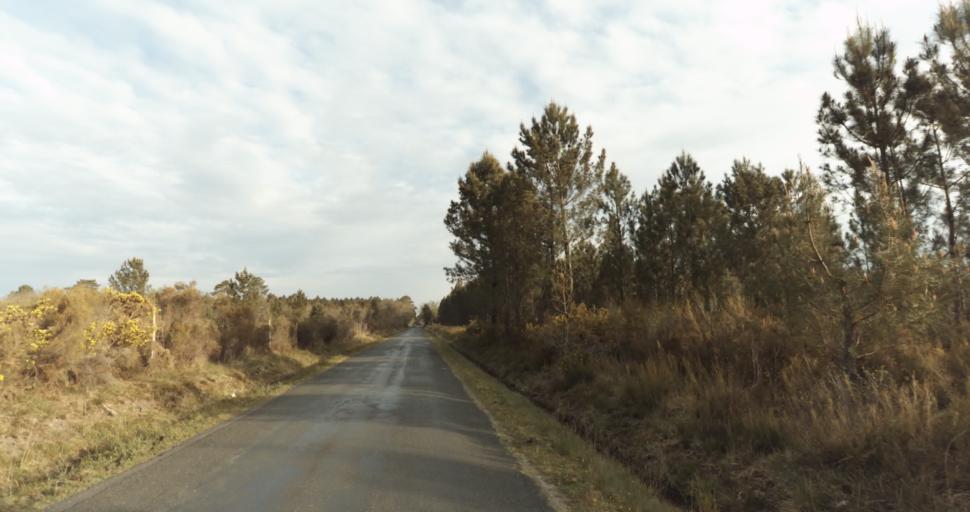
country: FR
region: Aquitaine
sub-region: Departement de la Gironde
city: Martignas-sur-Jalle
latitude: 44.7959
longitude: -0.7623
